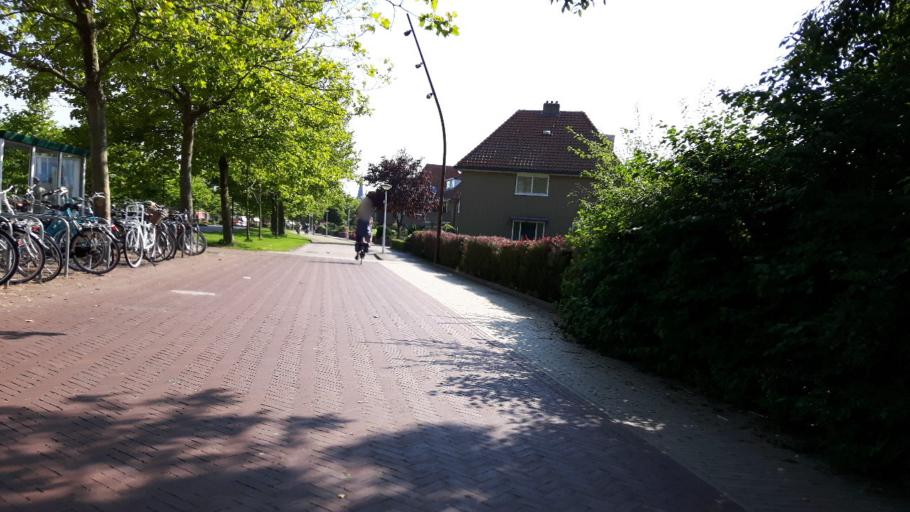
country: NL
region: Friesland
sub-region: Gemeente Franekeradeel
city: Franeker
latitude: 53.1931
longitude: 5.5406
